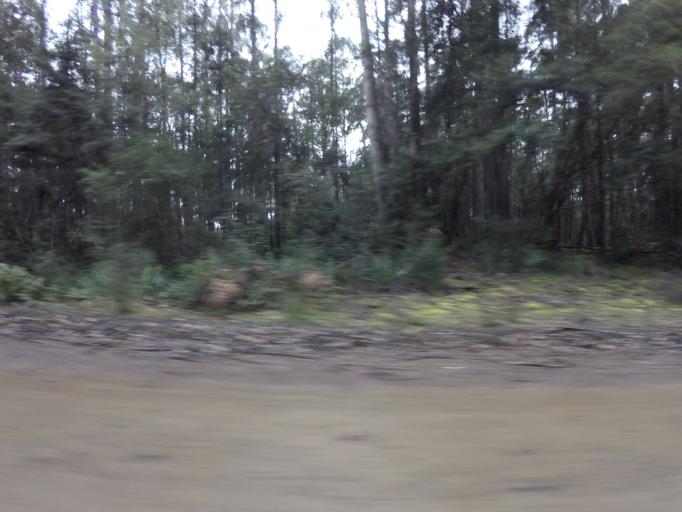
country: AU
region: Tasmania
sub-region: Huon Valley
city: Geeveston
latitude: -43.4802
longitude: 146.8907
